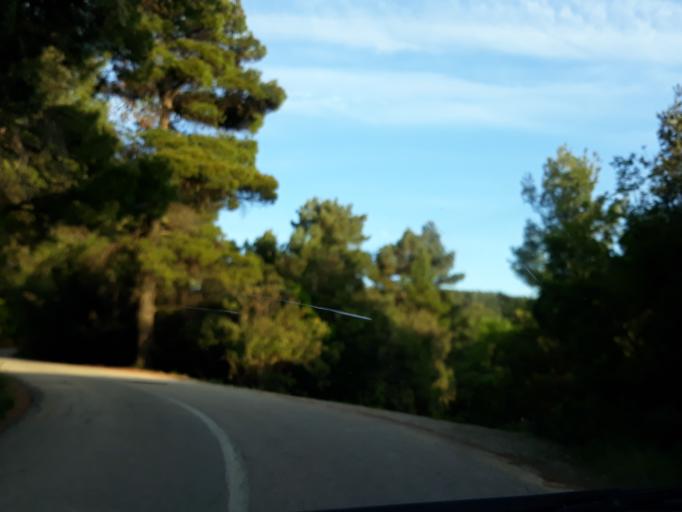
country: GR
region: Attica
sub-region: Nomarchia Anatolikis Attikis
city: Afidnes
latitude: 38.2187
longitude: 23.7796
